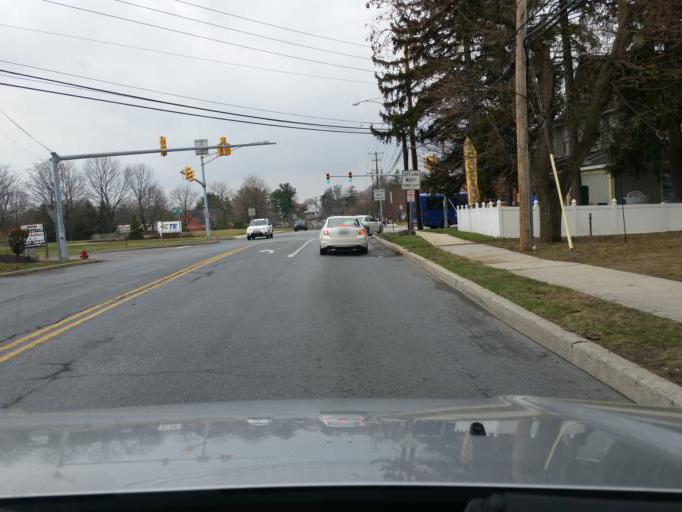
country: US
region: Pennsylvania
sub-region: Dauphin County
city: Paxtonia
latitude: 40.3193
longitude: -76.7871
